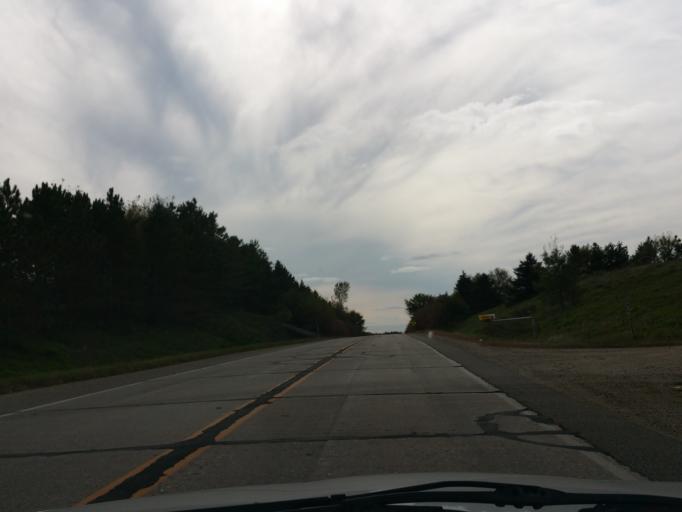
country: US
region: Wisconsin
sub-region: Pierce County
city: River Falls
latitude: 44.7996
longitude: -92.6782
